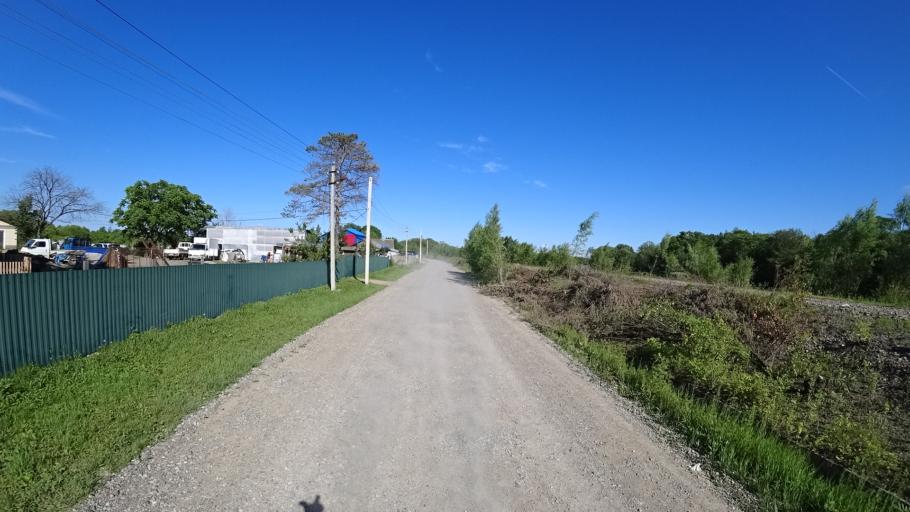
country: RU
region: Khabarovsk Krai
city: Khor
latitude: 47.8862
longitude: 135.0047
